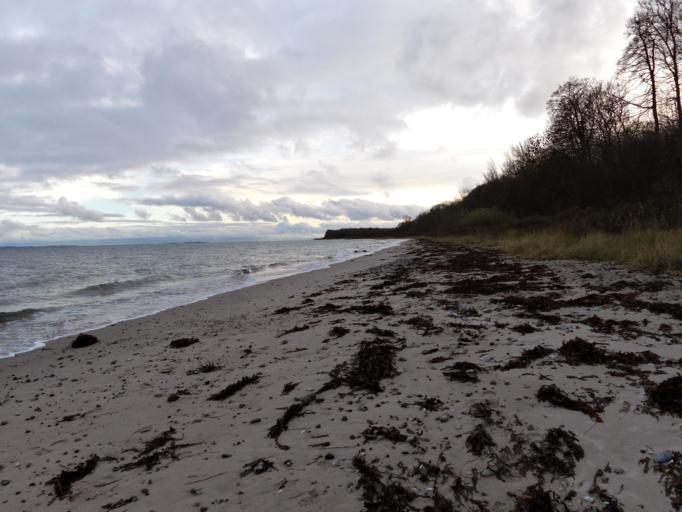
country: DK
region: Central Jutland
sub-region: Arhus Kommune
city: Beder
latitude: 56.0614
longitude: 10.2597
